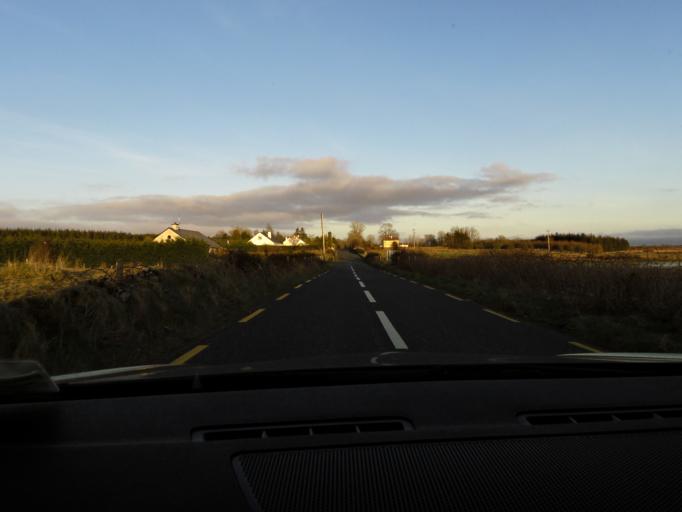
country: IE
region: Connaught
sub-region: Sligo
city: Tobercurry
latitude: 54.0513
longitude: -8.7064
